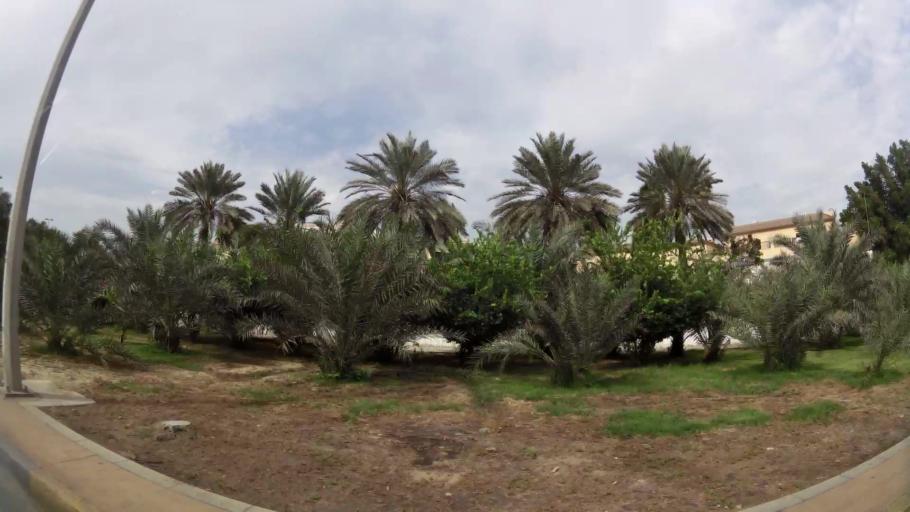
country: AE
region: Abu Dhabi
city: Abu Dhabi
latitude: 24.4555
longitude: 54.3676
